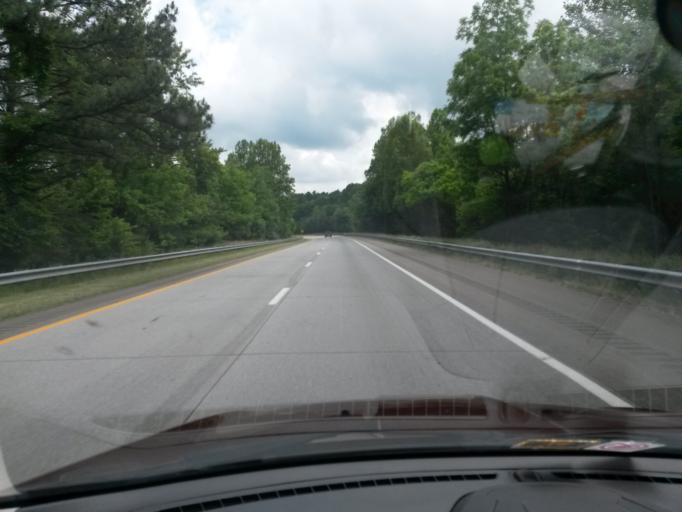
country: US
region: North Carolina
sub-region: Surry County
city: Elkin
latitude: 36.2663
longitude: -80.8257
